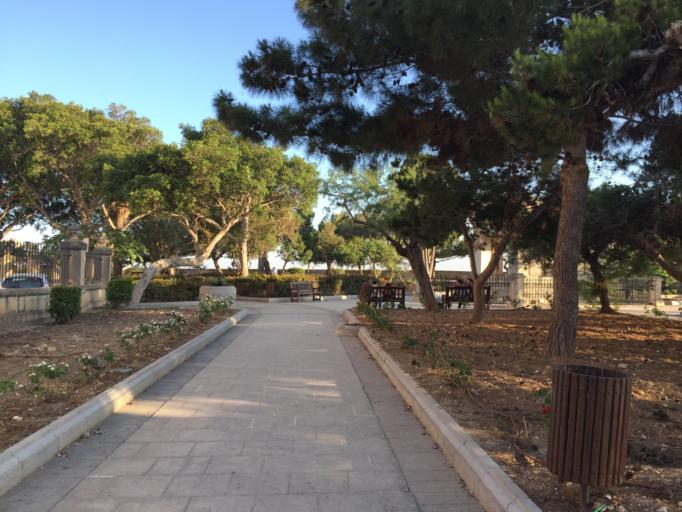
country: MT
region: Il-Furjana
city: Floriana
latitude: 35.8973
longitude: 14.5082
